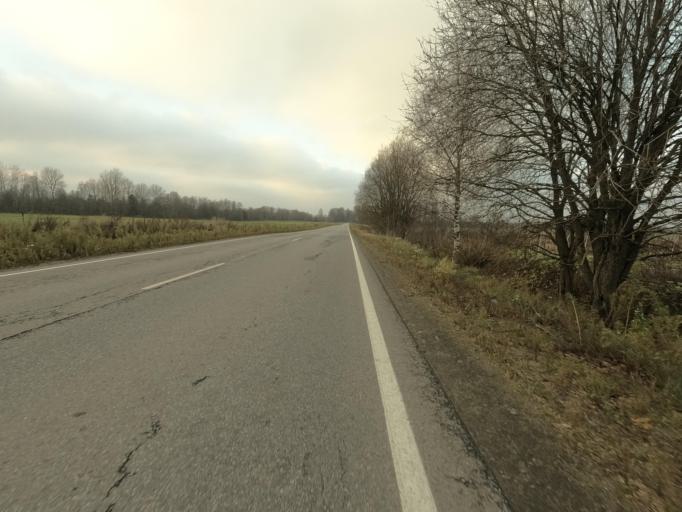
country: RU
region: Leningrad
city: Mga
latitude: 59.7688
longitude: 31.0208
